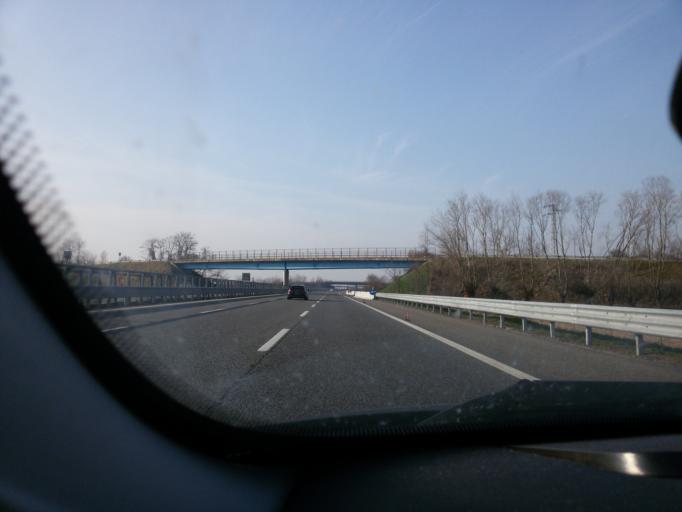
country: IT
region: Piedmont
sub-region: Provincia di Alessandria
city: Borgo San Martino
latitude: 45.1008
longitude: 8.4942
